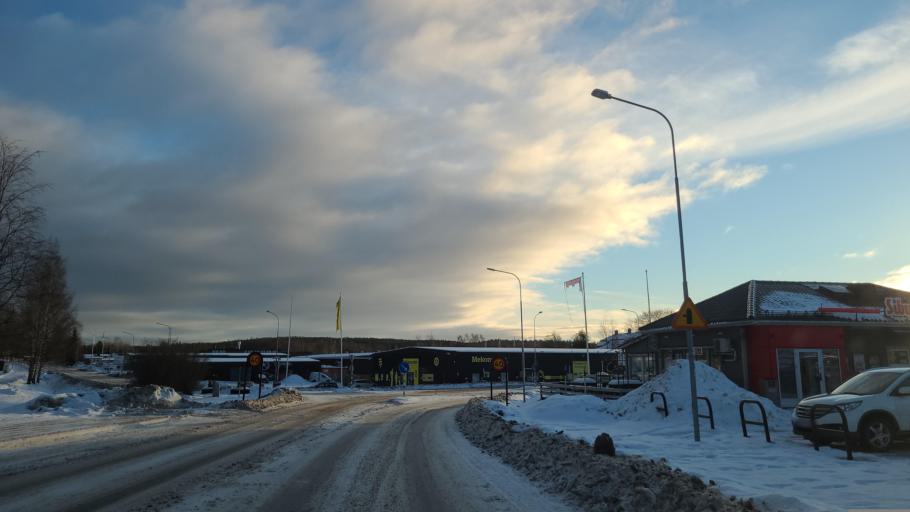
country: SE
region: Gaevleborg
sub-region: Bollnas Kommun
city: Bollnas
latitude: 61.3570
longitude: 16.4230
